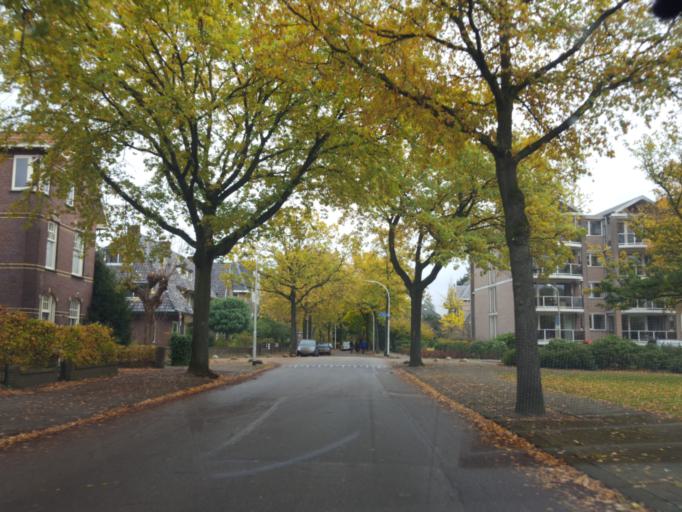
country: NL
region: Gelderland
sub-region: Gemeente Nijmegen
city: Nijmegen
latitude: 51.8413
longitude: 5.8348
